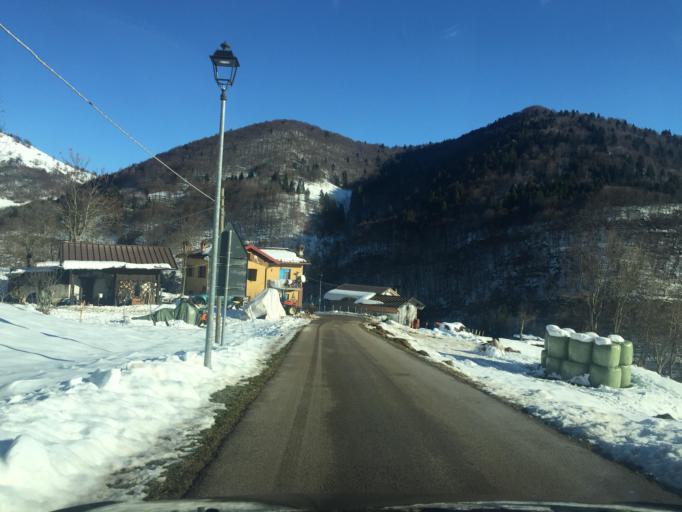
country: IT
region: Friuli Venezia Giulia
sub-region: Provincia di Udine
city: Lauco
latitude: 46.4387
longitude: 12.9663
